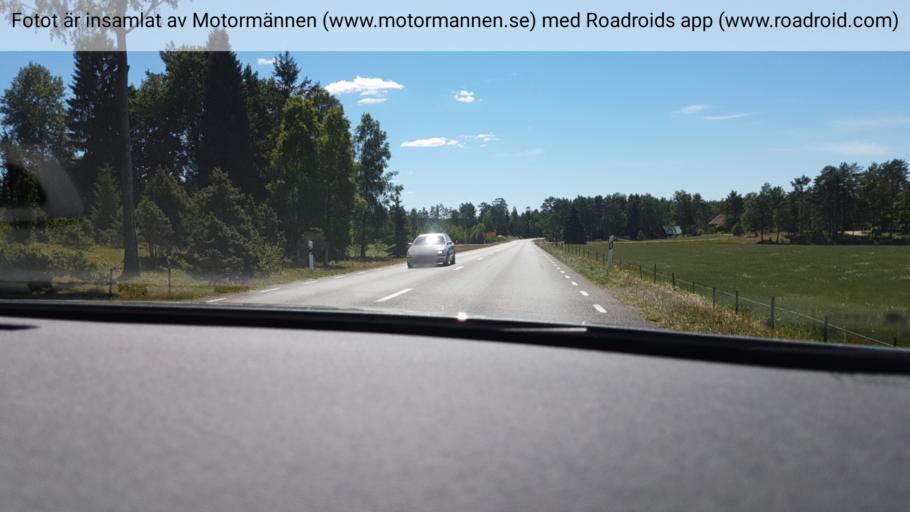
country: SE
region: Joenkoeping
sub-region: Gnosjo Kommun
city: Marieholm
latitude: 57.6482
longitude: 13.8084
